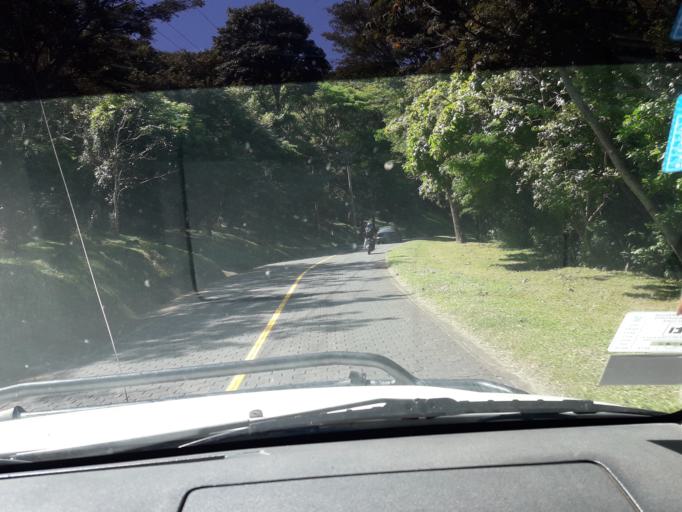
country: NI
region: Rivas
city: Cardenas
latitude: 11.2348
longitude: -85.5633
